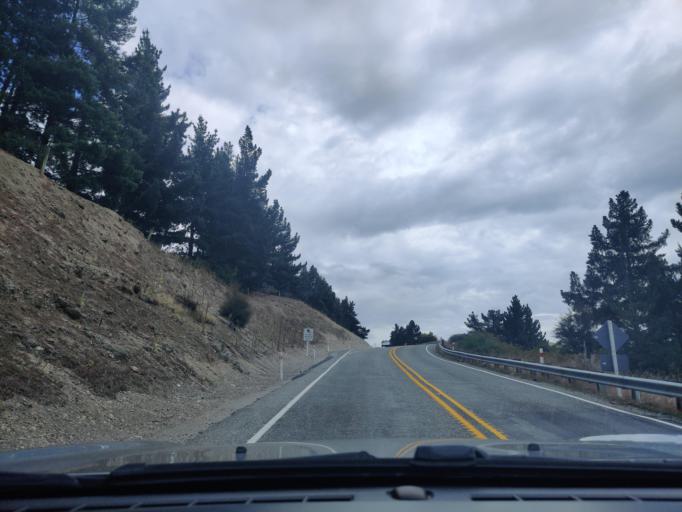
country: NZ
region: Otago
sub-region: Queenstown-Lakes District
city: Wanaka
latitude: -44.7315
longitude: 169.2546
